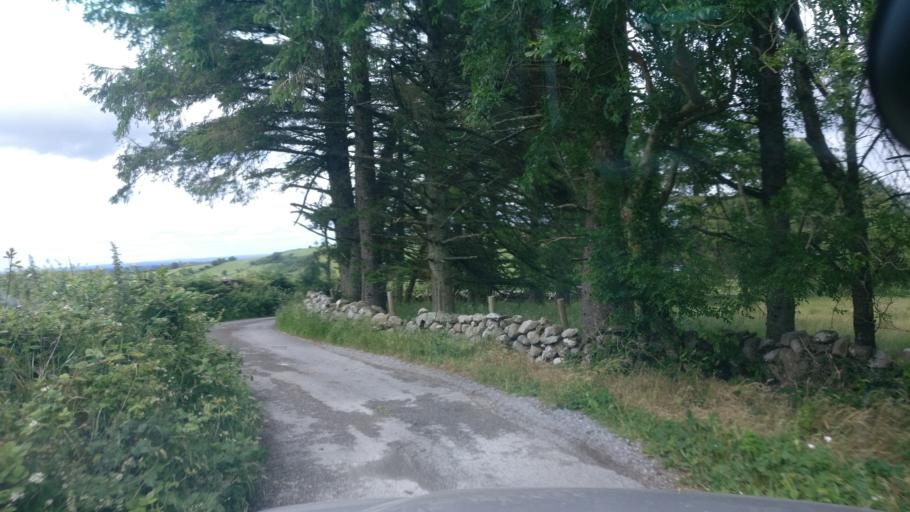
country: IE
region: Connaught
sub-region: County Galway
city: Loughrea
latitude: 53.1525
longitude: -8.5570
